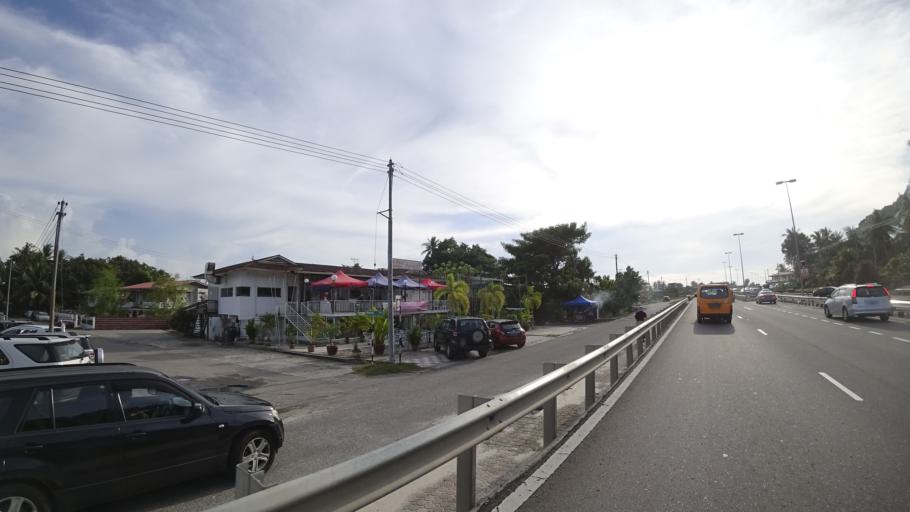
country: BN
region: Brunei and Muara
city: Bandar Seri Begawan
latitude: 4.8527
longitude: 114.8855
